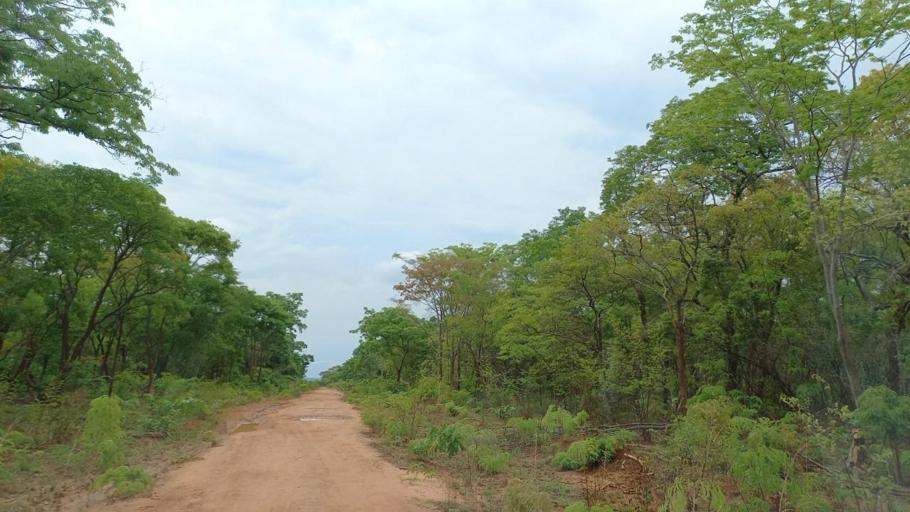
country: ZM
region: North-Western
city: Kalengwa
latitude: -13.6157
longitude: 24.9760
